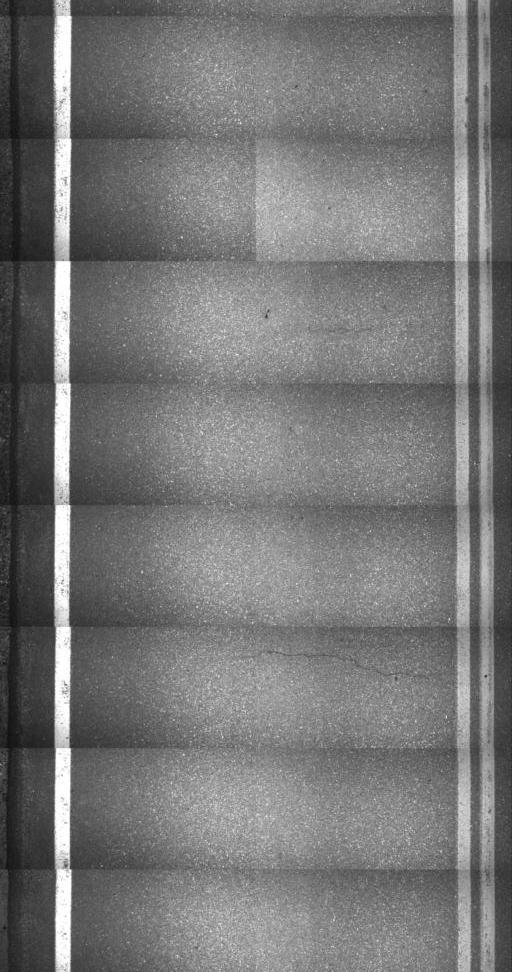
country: US
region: Vermont
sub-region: Caledonia County
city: Lyndonville
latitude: 44.7596
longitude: -72.0522
